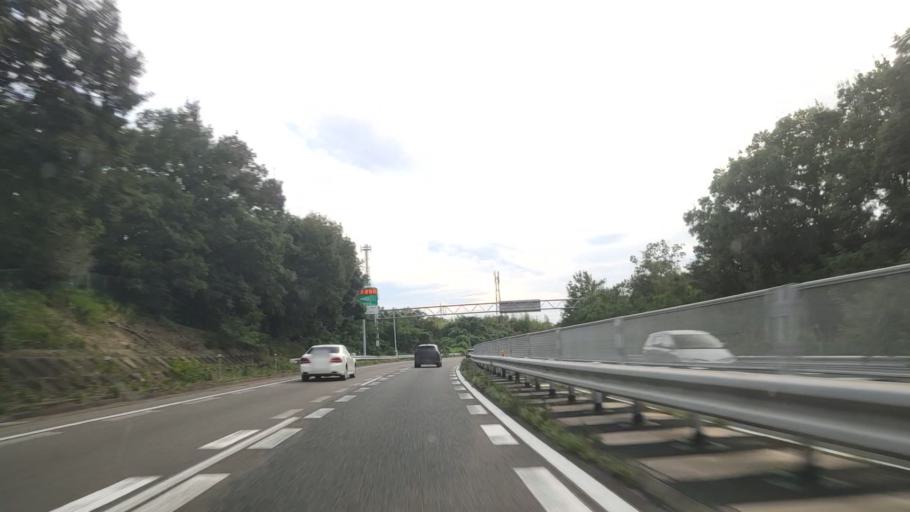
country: JP
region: Aichi
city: Kasugai
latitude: 35.3123
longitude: 137.0173
